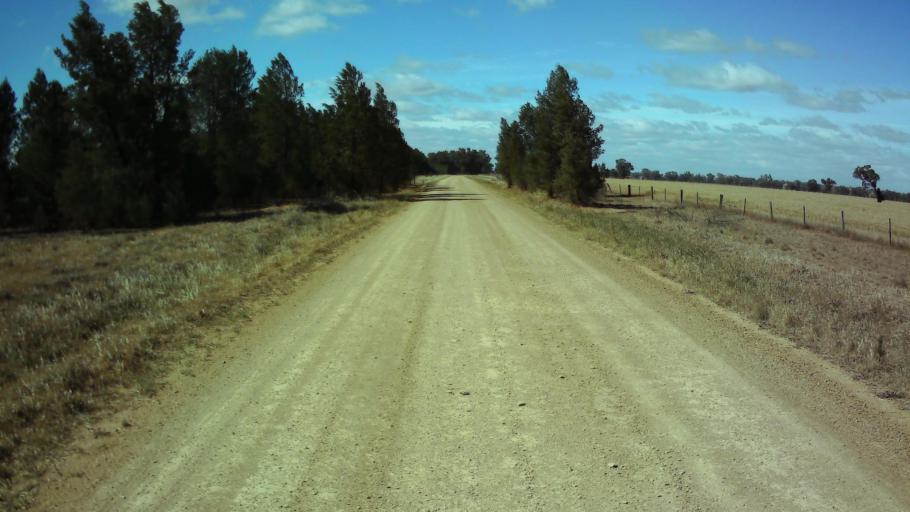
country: AU
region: New South Wales
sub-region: Weddin
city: Grenfell
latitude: -34.0312
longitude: 148.3174
